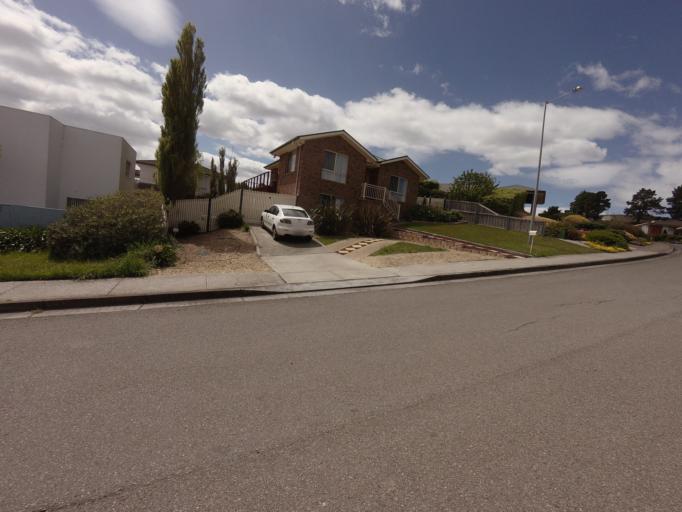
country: AU
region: Tasmania
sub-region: Clarence
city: Howrah
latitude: -42.8897
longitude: 147.4223
